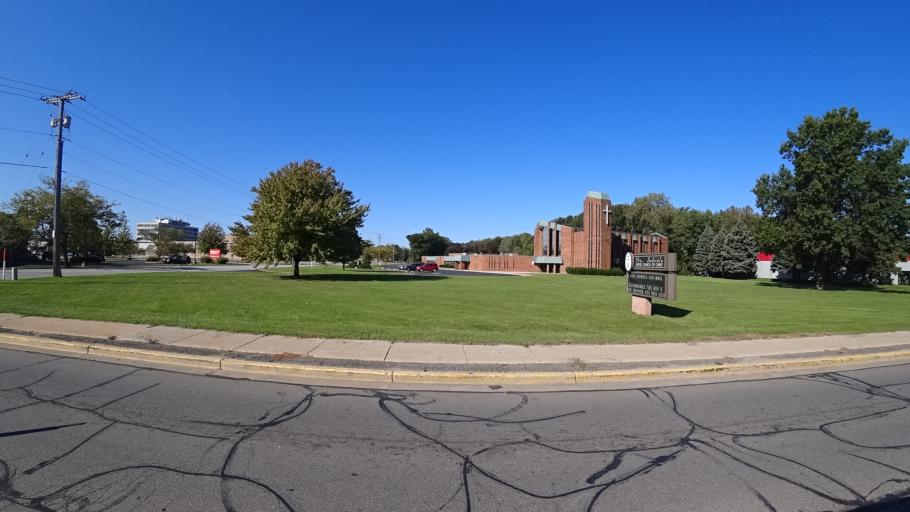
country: US
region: Indiana
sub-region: LaPorte County
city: Michigan City
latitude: 41.6843
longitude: -86.8940
